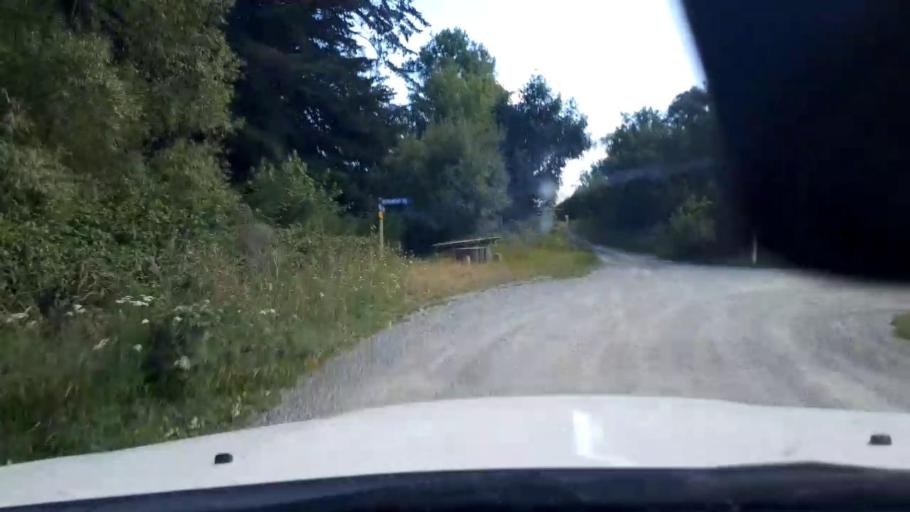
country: NZ
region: Canterbury
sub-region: Timaru District
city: Pleasant Point
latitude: -44.0210
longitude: 170.7432
